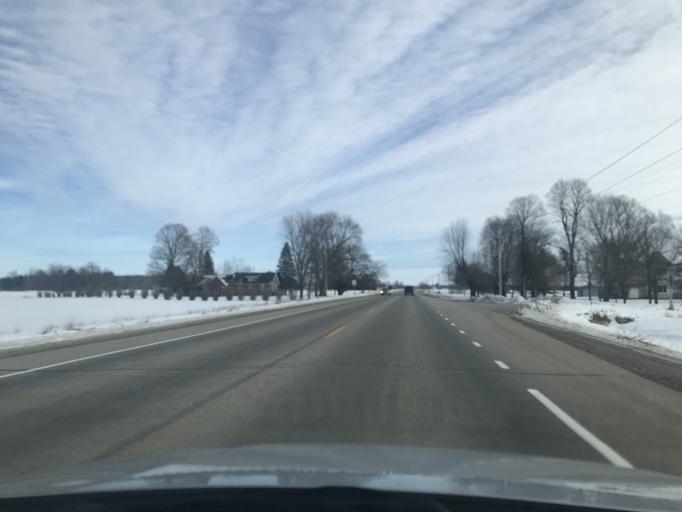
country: US
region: Wisconsin
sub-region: Oconto County
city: Gillett
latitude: 44.8962
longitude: -88.2677
